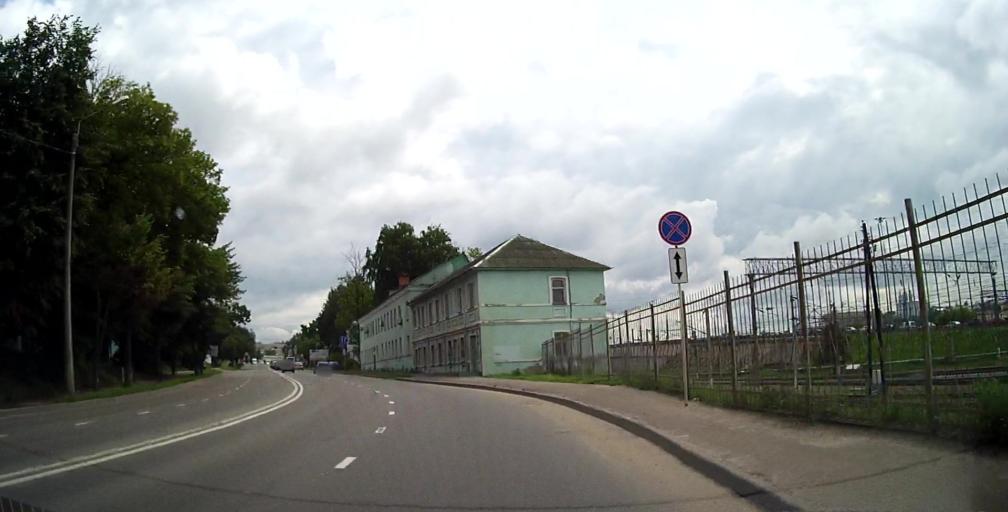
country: RU
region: Smolensk
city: Smolensk
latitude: 54.7987
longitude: 32.0404
